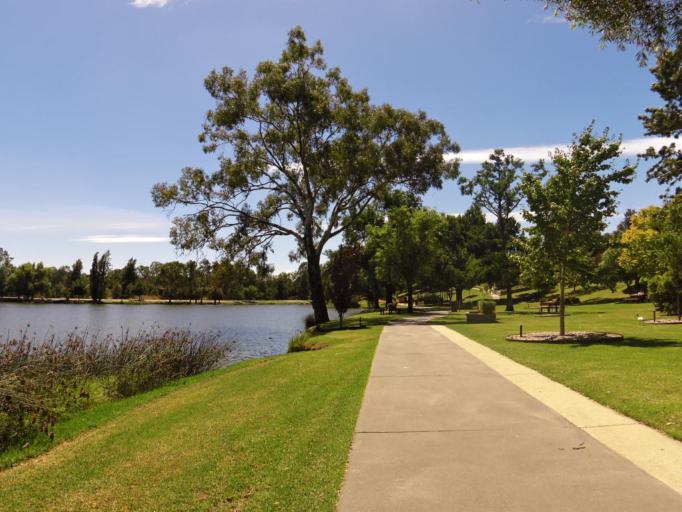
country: AU
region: Victoria
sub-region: Wodonga
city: Wodonga
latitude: -36.1134
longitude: 146.8905
